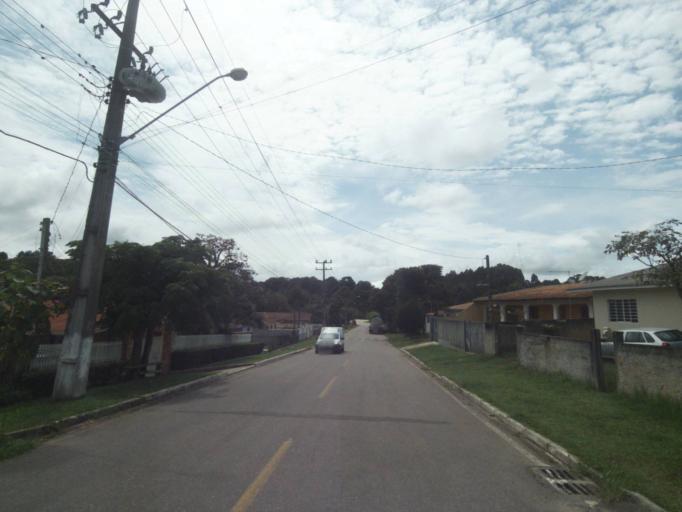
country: BR
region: Parana
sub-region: Campina Grande Do Sul
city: Campina Grande do Sul
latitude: -25.3080
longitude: -49.0503
